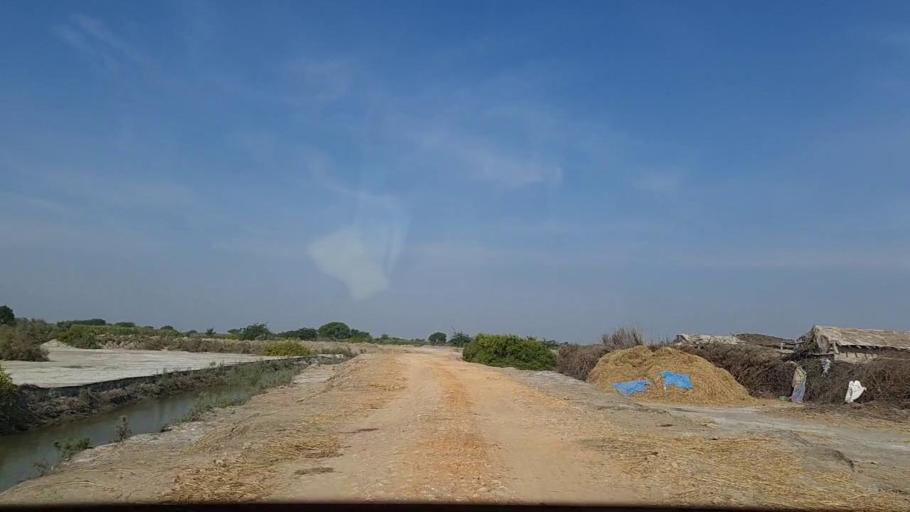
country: PK
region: Sindh
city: Daro Mehar
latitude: 24.7082
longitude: 68.1499
